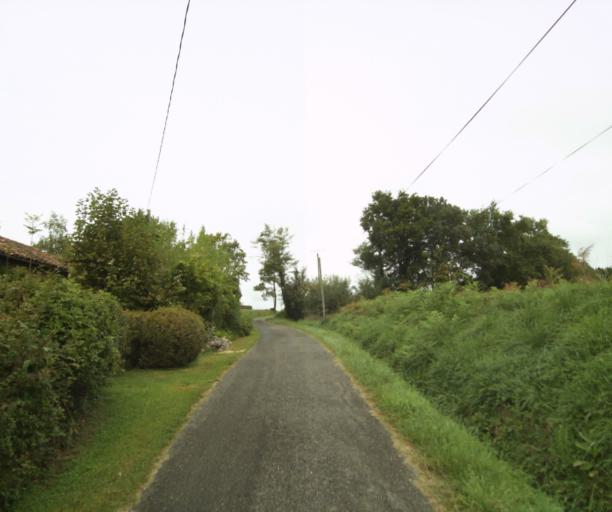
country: FR
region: Midi-Pyrenees
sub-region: Departement du Gers
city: Cazaubon
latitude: 43.8755
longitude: -0.0922
